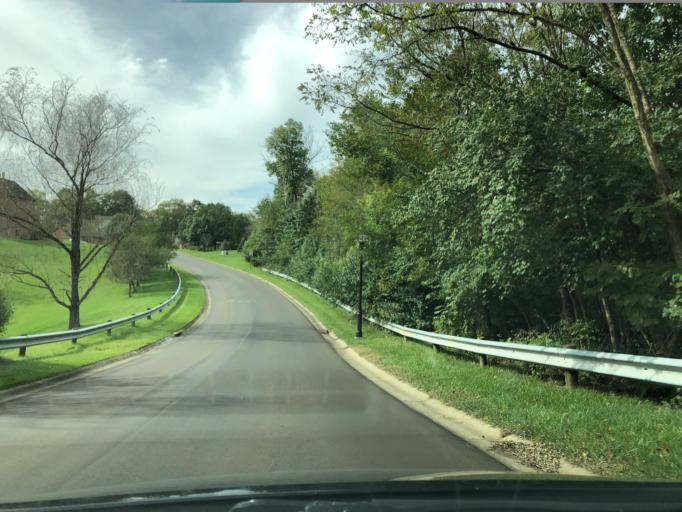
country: US
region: Ohio
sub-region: Hamilton County
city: Loveland
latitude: 39.2481
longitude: -84.2635
